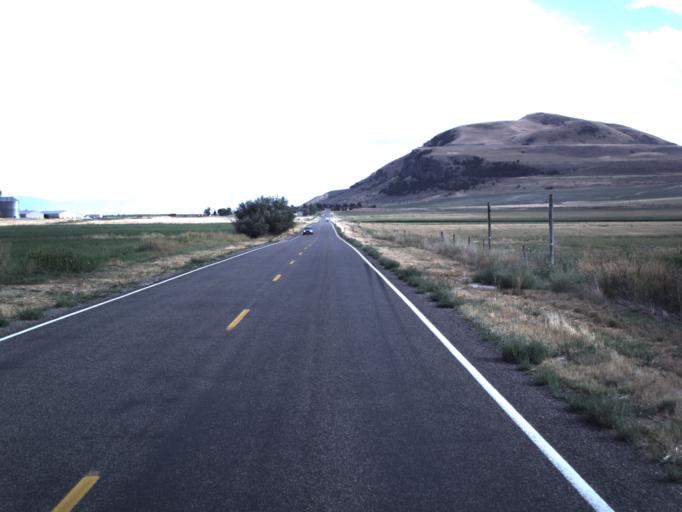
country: US
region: Utah
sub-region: Cache County
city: Lewiston
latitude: 41.9287
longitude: -111.9532
